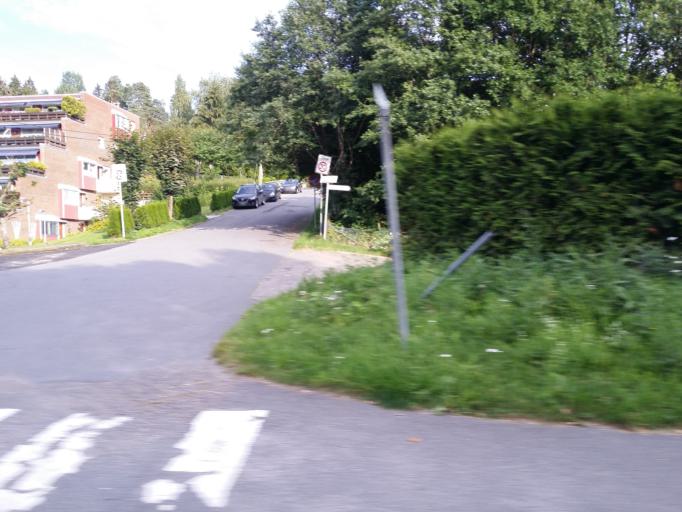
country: NO
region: Akershus
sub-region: Oppegard
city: Kolbotn
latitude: 59.8903
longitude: 10.8540
